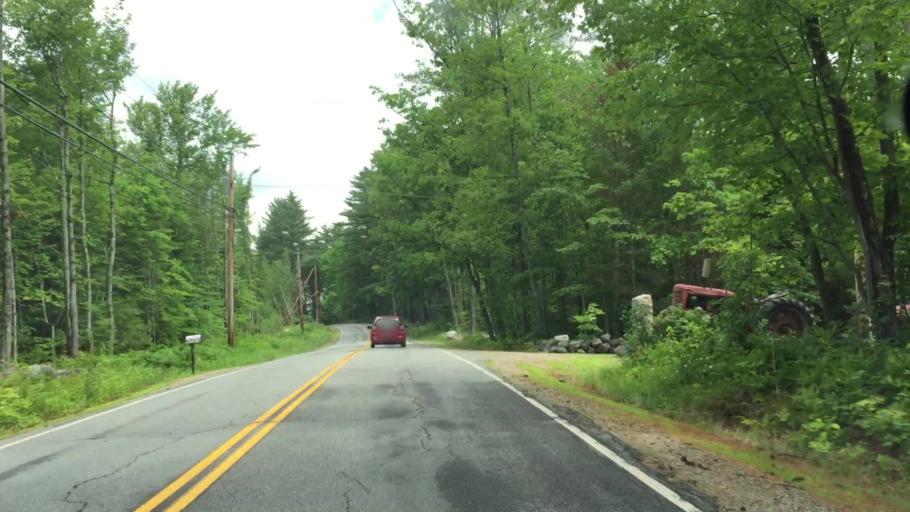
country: US
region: New Hampshire
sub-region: Carroll County
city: Sandwich
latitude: 43.7961
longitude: -71.4450
